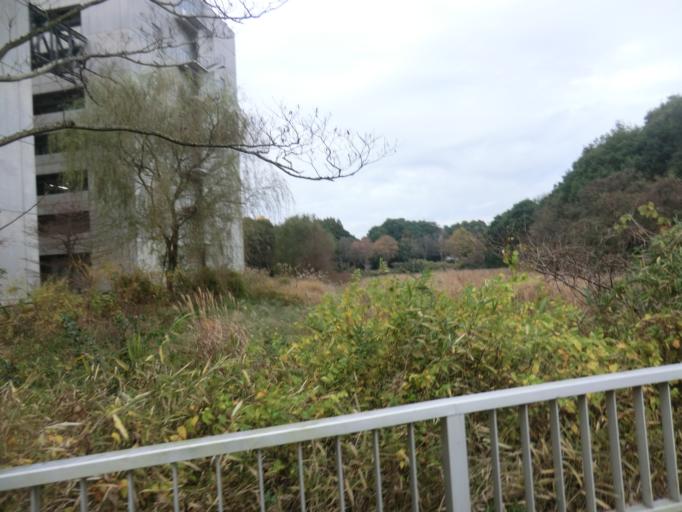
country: JP
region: Ibaraki
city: Naka
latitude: 36.0978
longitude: 140.1031
